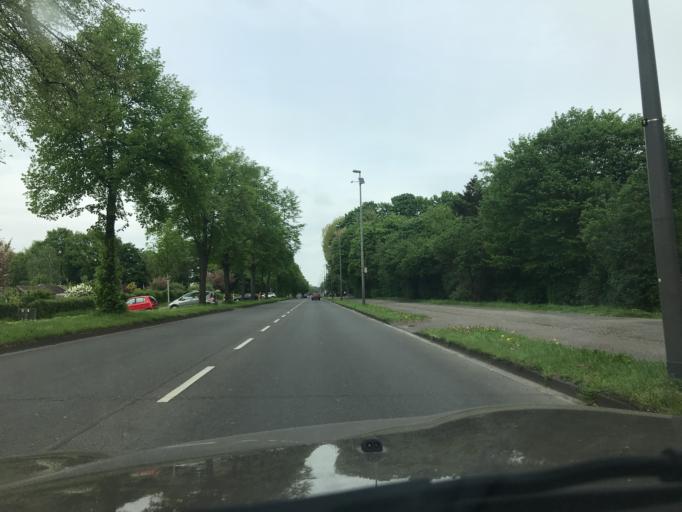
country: DE
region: North Rhine-Westphalia
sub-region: Regierungsbezirk Koln
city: Bilderstoeckchen
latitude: 50.9616
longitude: 6.9070
